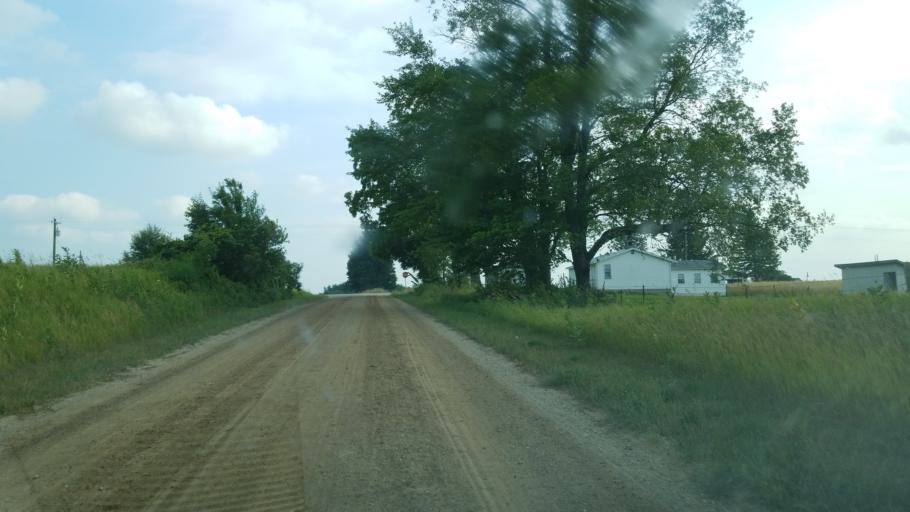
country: US
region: Michigan
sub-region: Mecosta County
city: Canadian Lakes
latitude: 43.5435
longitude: -85.3632
